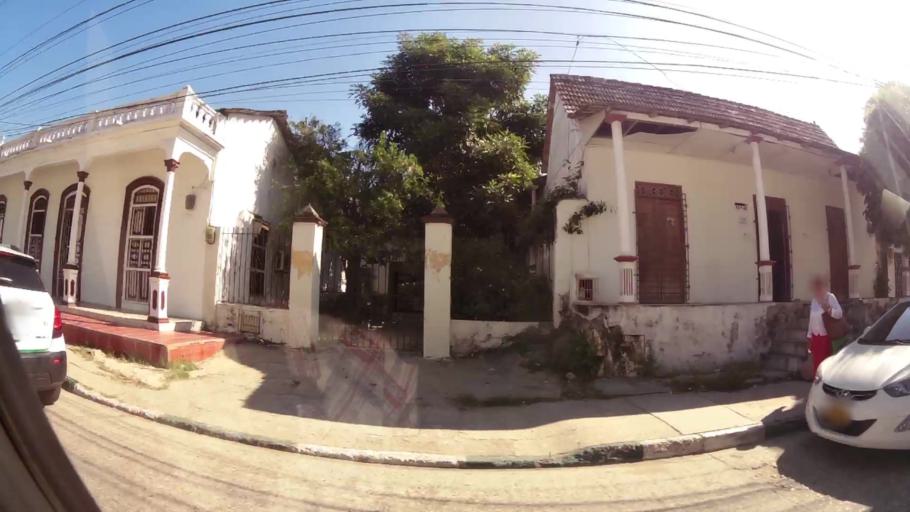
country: CO
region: Bolivar
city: Cartagena
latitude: 10.4312
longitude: -75.5356
